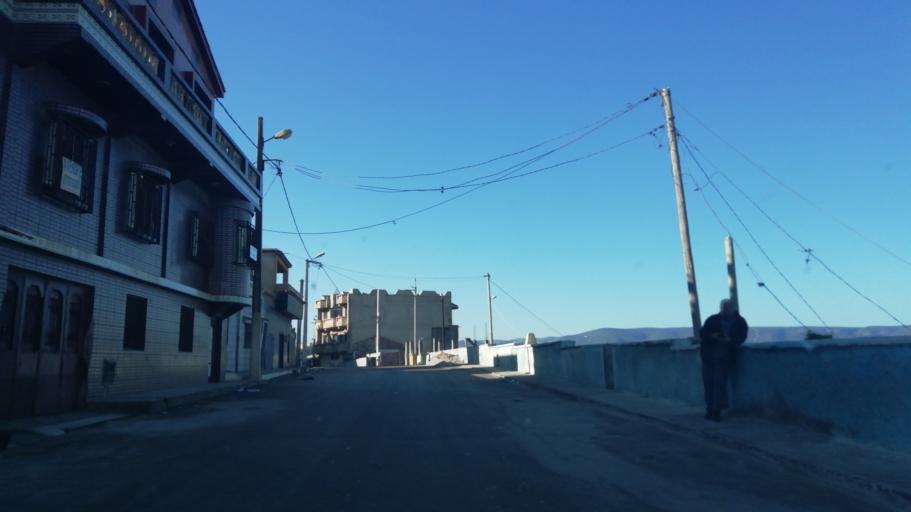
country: DZ
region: Oran
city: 'Ain el Turk
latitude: 35.7262
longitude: -0.8483
